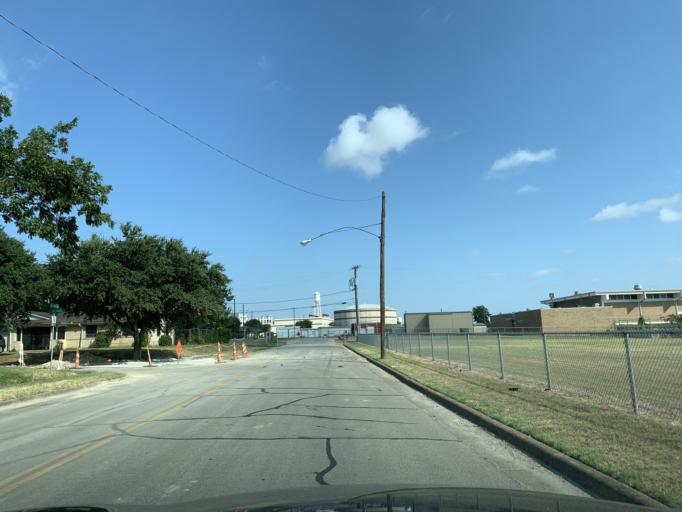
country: US
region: Texas
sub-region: Dallas County
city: Hutchins
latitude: 32.6928
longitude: -96.7851
